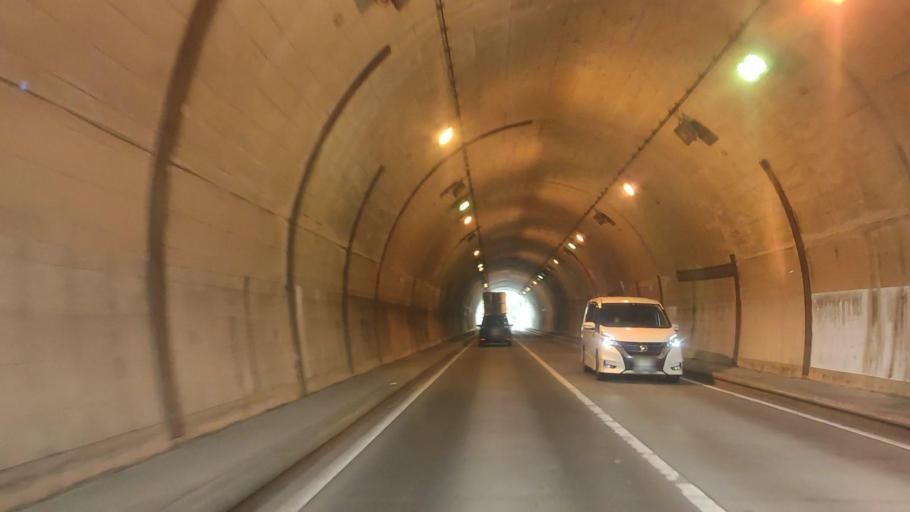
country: JP
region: Nagasaki
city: Shimabara
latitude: 32.8490
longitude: 130.2310
